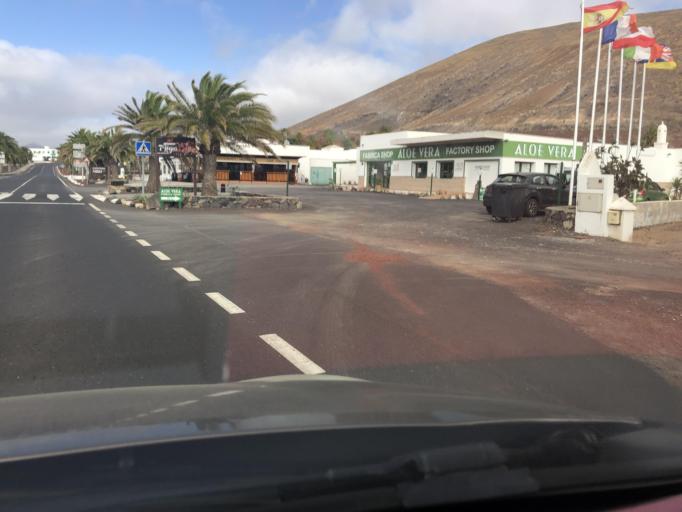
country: ES
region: Canary Islands
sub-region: Provincia de Las Palmas
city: Yaiza
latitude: 28.9529
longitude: -13.7769
